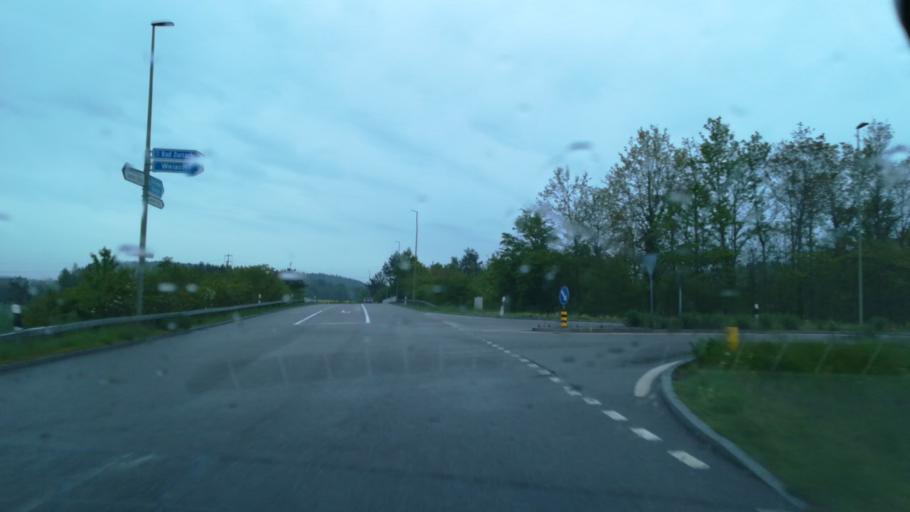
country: CH
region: Zurich
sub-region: Bezirk Buelach
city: Glattfelden
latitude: 47.5677
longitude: 8.4724
